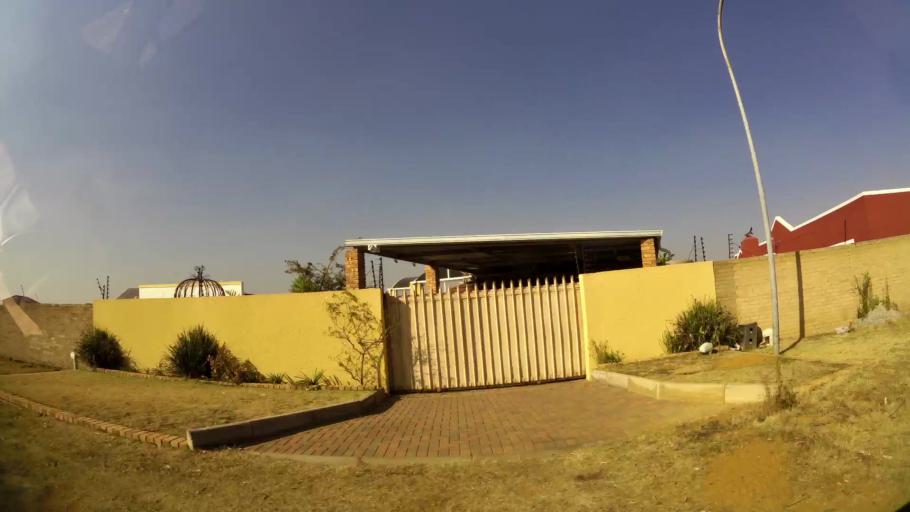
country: ZA
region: Gauteng
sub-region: West Rand District Municipality
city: Randfontein
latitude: -26.1810
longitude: 27.6782
